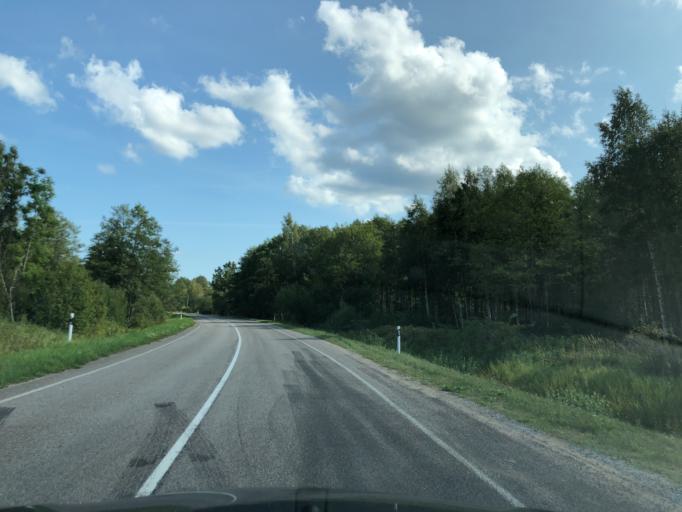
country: EE
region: Hiiumaa
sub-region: Kaerdla linn
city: Kardla
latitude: 58.7193
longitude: 22.5645
